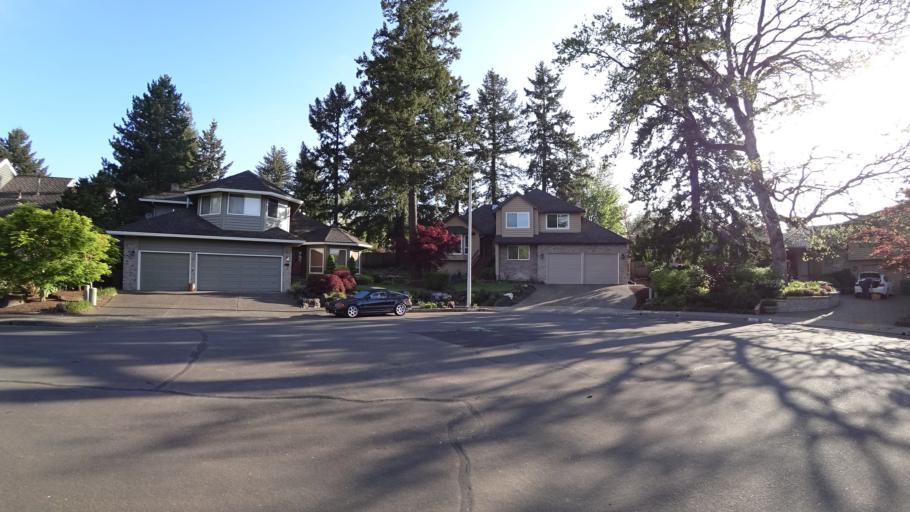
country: US
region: Oregon
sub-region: Washington County
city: Beaverton
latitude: 45.4463
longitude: -122.8163
